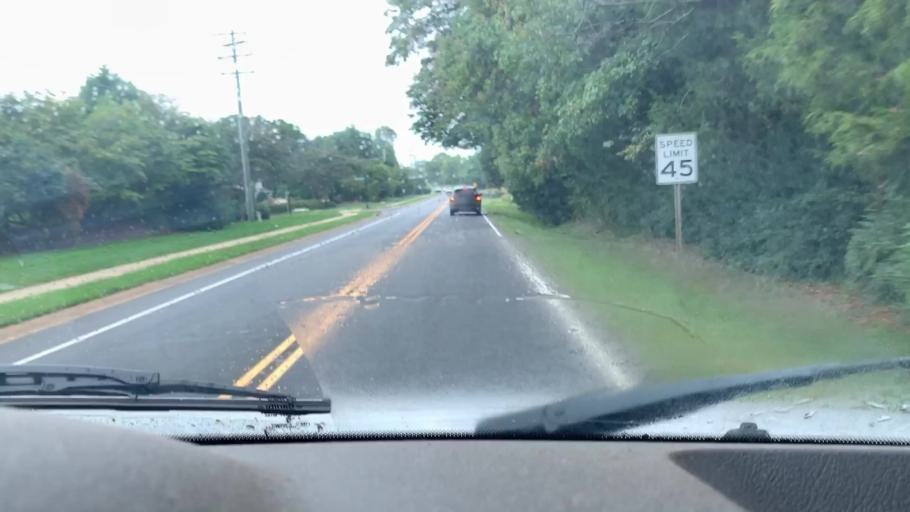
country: US
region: North Carolina
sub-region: Mecklenburg County
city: Cornelius
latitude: 35.4829
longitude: -80.8925
